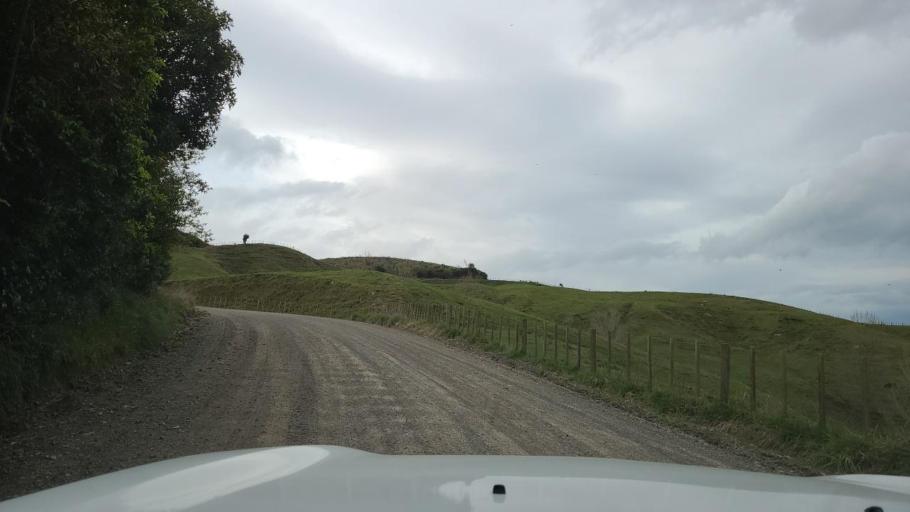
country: NZ
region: Hawke's Bay
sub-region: Napier City
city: Napier
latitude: -39.1861
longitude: 176.9446
